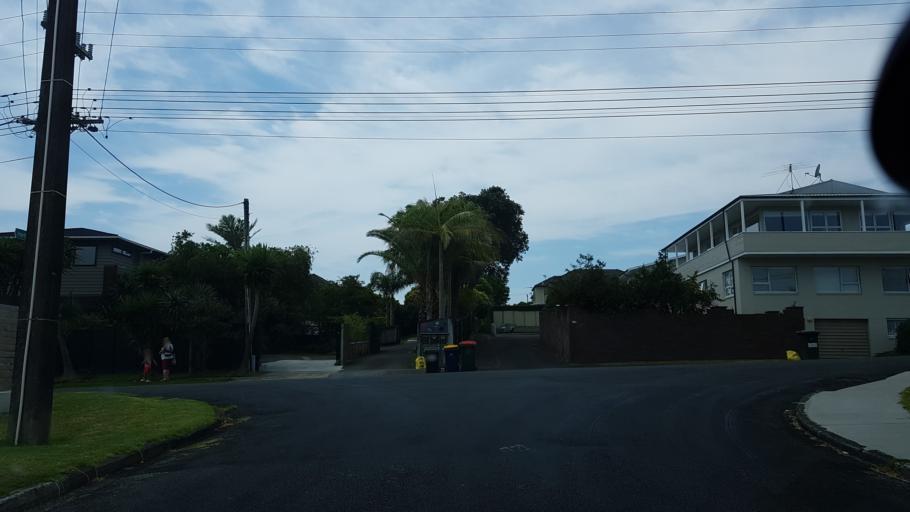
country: NZ
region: Auckland
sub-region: Auckland
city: North Shore
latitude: -36.8023
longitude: 174.7723
